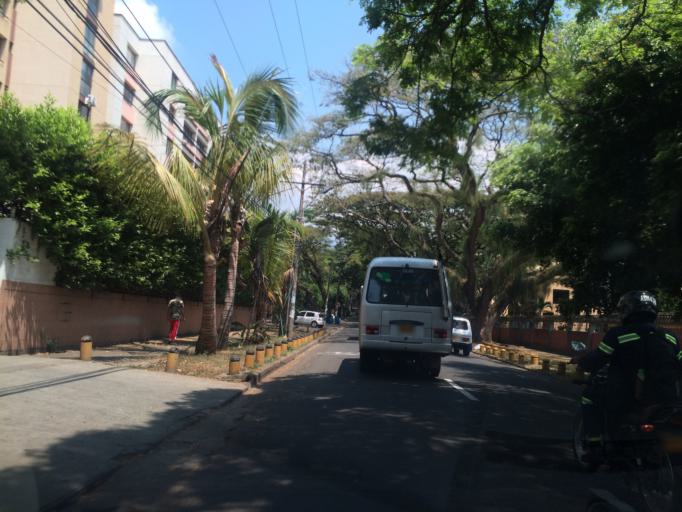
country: CO
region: Valle del Cauca
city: Cali
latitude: 3.4091
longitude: -76.5488
